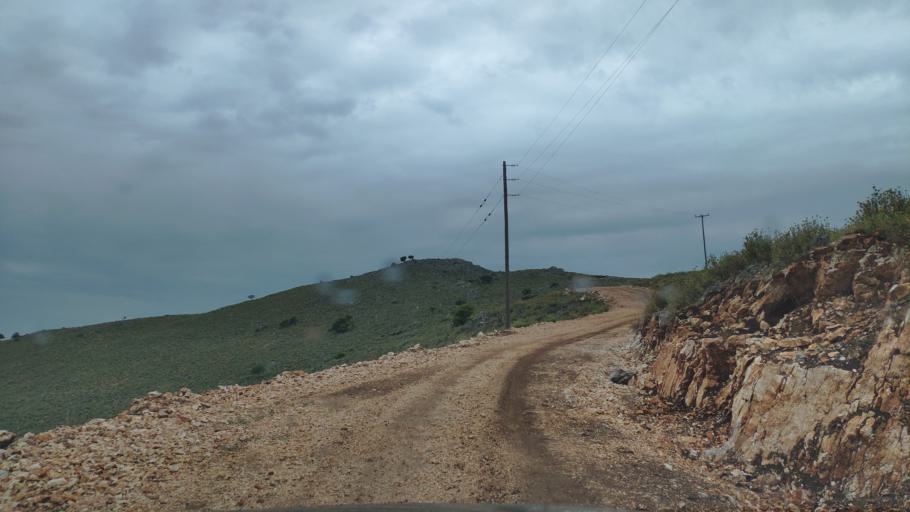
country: GR
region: West Greece
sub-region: Nomos Aitolias kai Akarnanias
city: Archontochorion
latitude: 38.6871
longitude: 21.0348
